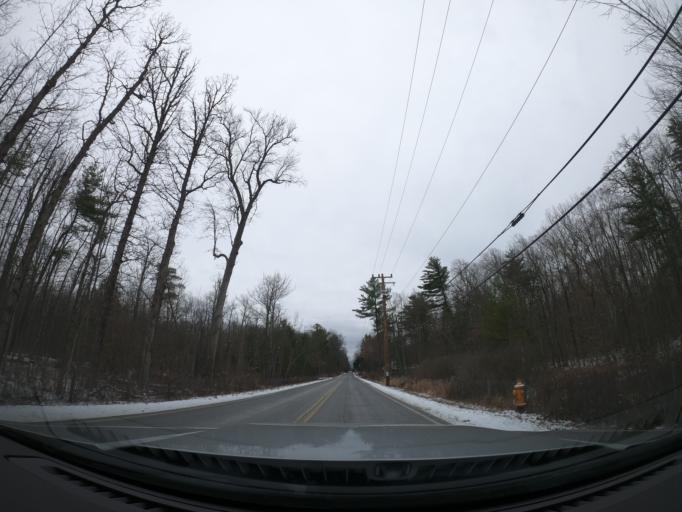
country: US
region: New York
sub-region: Tompkins County
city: Northeast Ithaca
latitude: 42.4751
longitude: -76.4504
